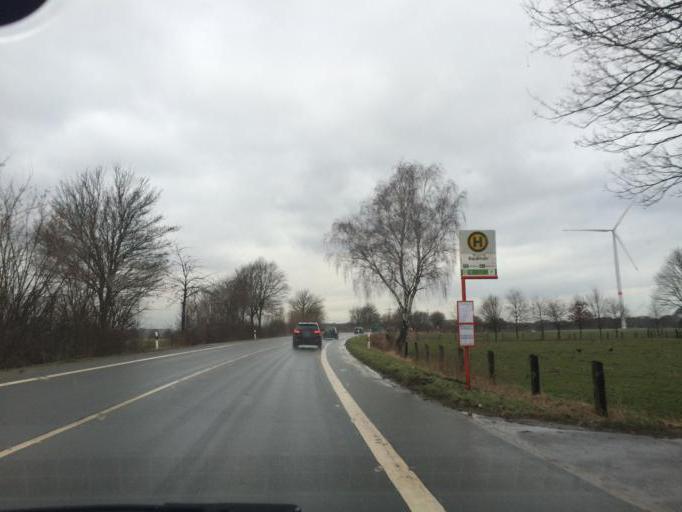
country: DE
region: North Rhine-Westphalia
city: Dorsten
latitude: 51.6169
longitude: 6.9533
